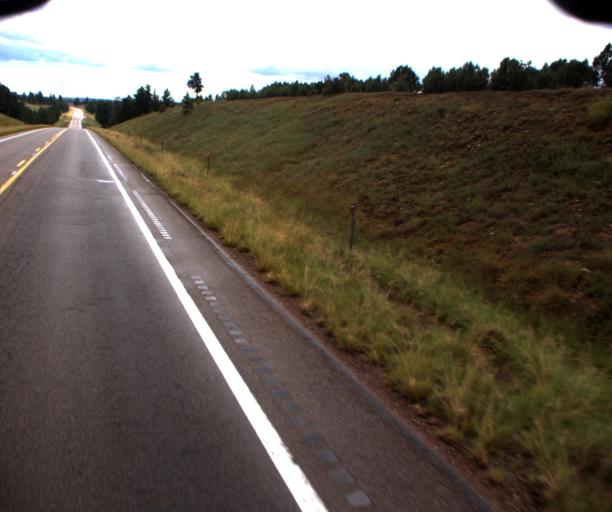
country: US
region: Arizona
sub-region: Navajo County
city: Heber-Overgaard
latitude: 34.3748
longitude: -110.4623
